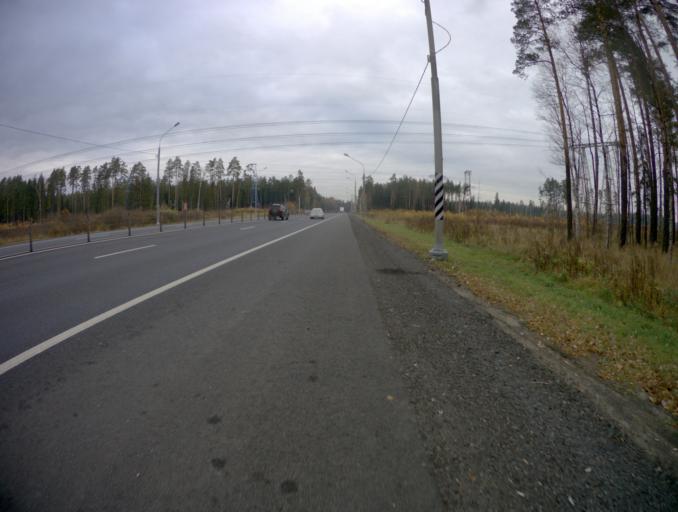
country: RU
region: Moskovskaya
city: Malaya Dubna
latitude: 55.8522
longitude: 38.9634
